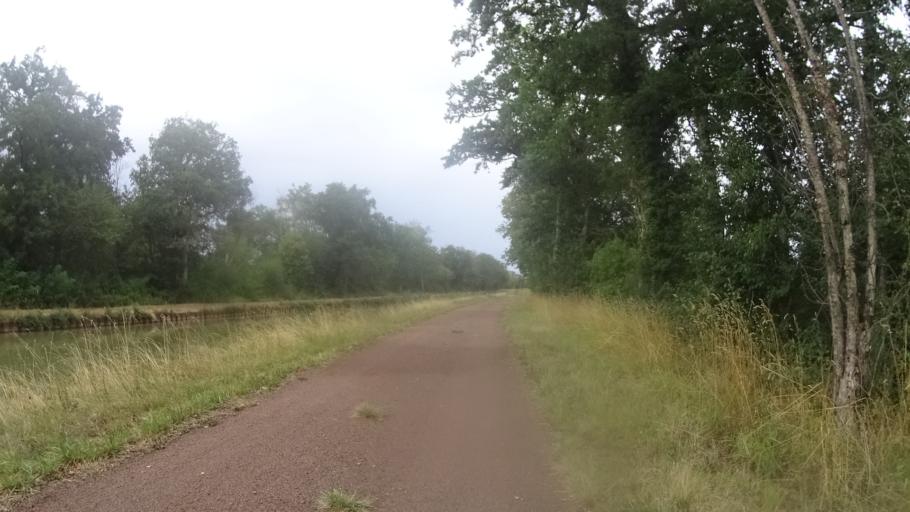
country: FR
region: Bourgogne
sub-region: Departement de la Nievre
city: Imphy
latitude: 46.9031
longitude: 3.2463
